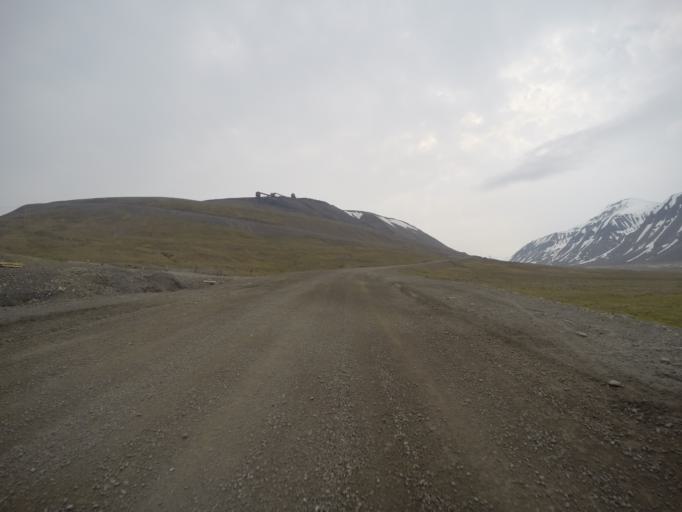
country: SJ
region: Svalbard
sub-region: Spitsbergen
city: Longyearbyen
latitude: 78.1612
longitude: 16.0037
